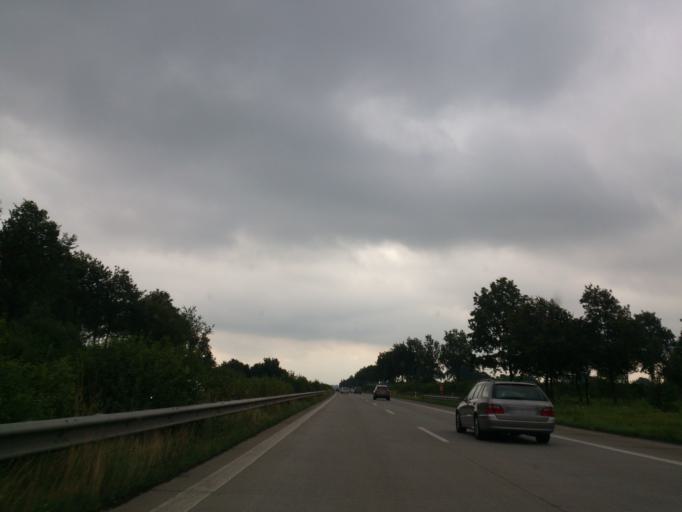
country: DE
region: Schleswig-Holstein
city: Hohenfelde
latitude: 53.8433
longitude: 9.5999
